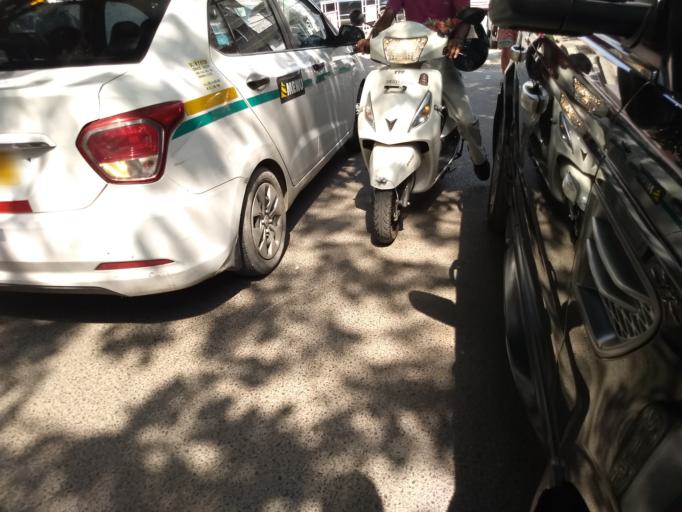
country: IN
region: NCT
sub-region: New Delhi
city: New Delhi
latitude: 28.5588
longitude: 77.2010
